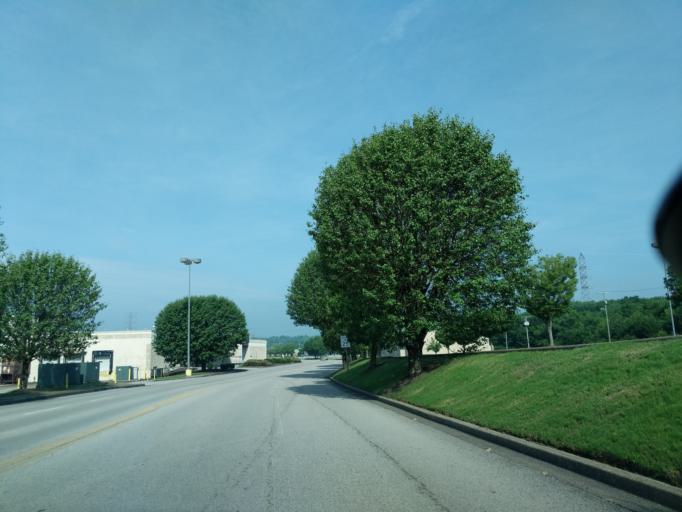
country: US
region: Tennessee
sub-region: Davidson County
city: Goodlettsville
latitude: 36.3048
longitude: -86.6954
